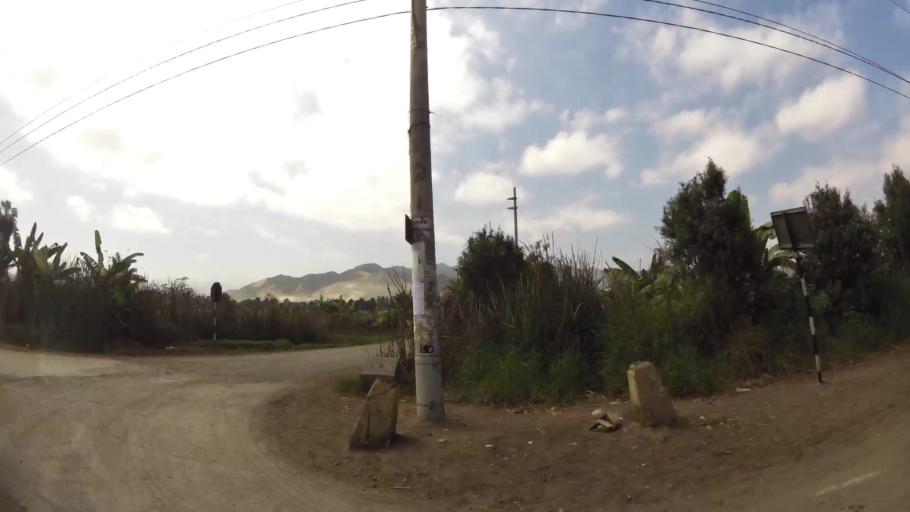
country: PE
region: Lima
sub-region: Provincia de Canete
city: Mala
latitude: -12.6951
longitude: -76.6243
